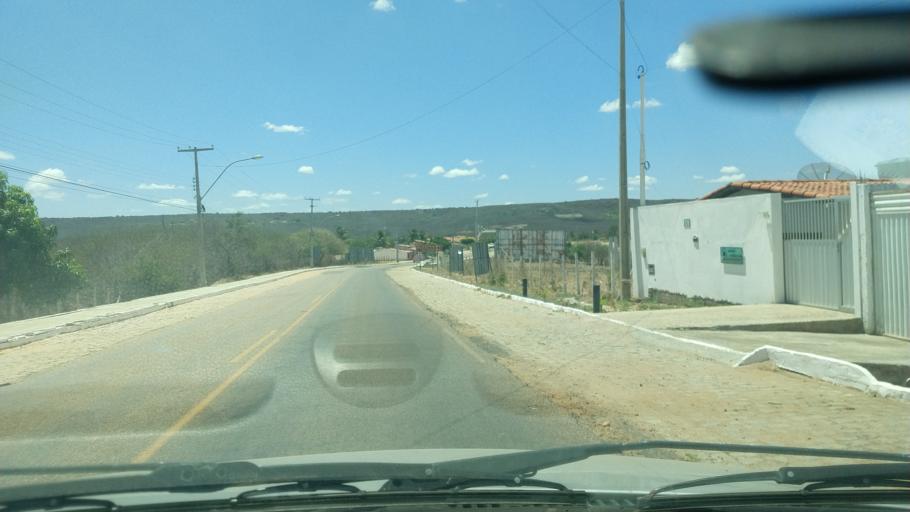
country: BR
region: Rio Grande do Norte
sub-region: Cerro Cora
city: Cerro Cora
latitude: -6.0547
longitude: -36.3570
